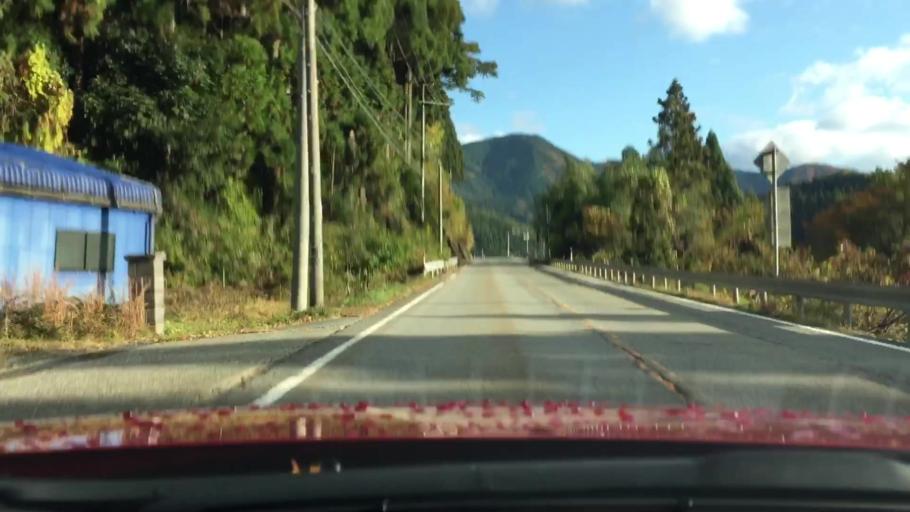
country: JP
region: Hyogo
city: Yamazakicho-nakabirose
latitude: 35.1776
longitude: 134.5374
